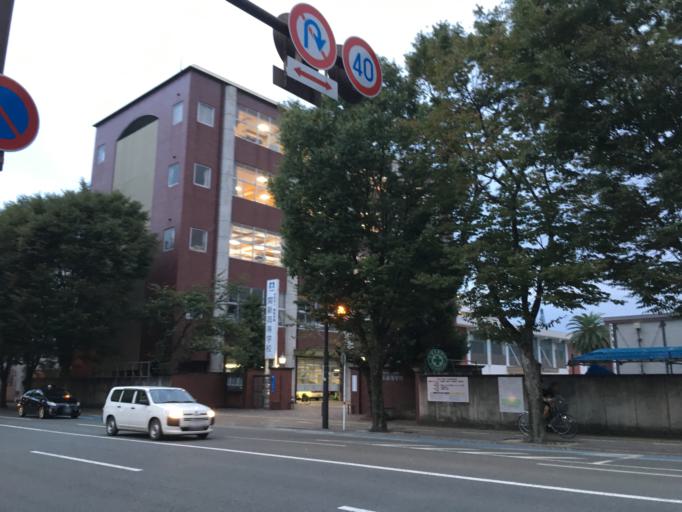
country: JP
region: Kumamoto
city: Kumamoto
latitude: 32.8003
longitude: 130.7275
